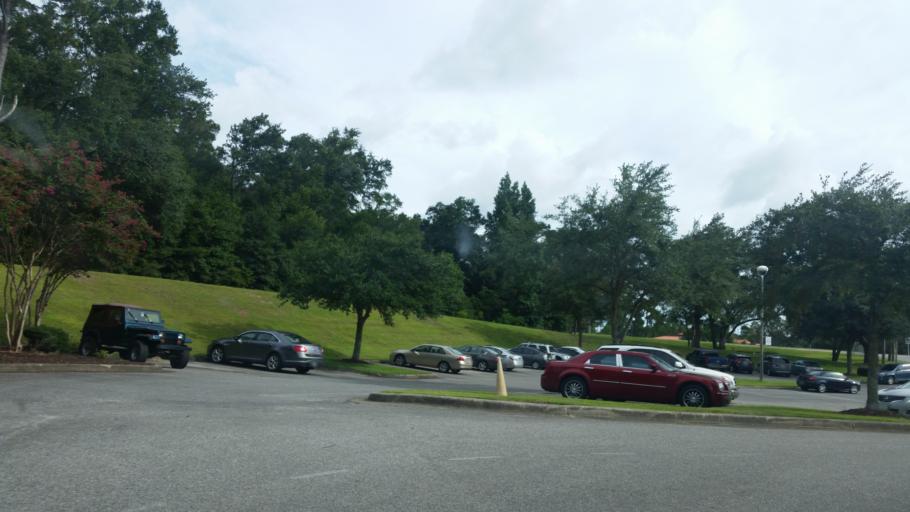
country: US
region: Florida
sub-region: Escambia County
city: Ferry Pass
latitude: 30.5336
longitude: -87.2184
